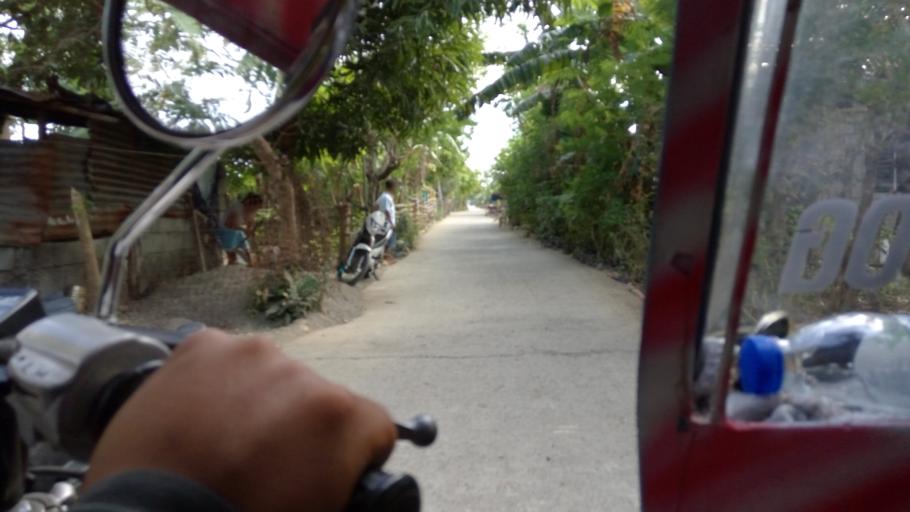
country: PH
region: Ilocos
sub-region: Province of La Union
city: San Eugenio
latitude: 16.3574
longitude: 120.3526
